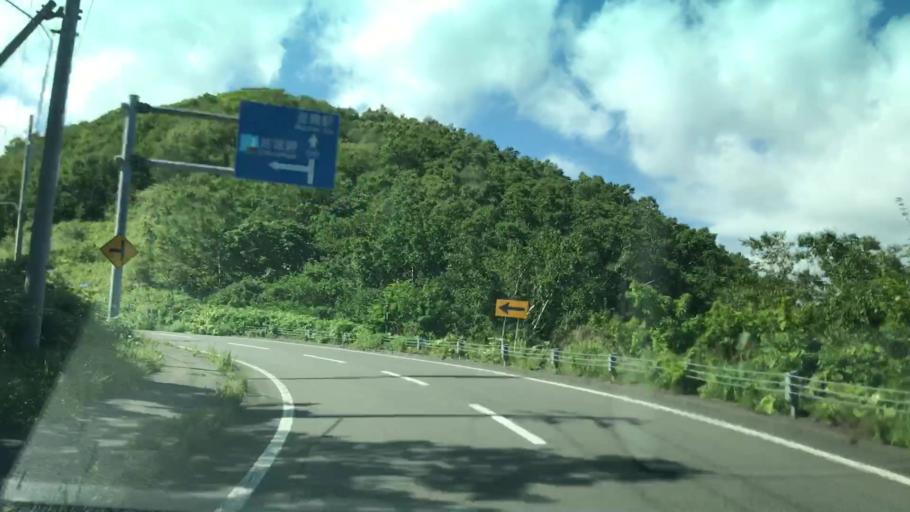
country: JP
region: Hokkaido
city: Muroran
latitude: 42.3049
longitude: 140.9995
